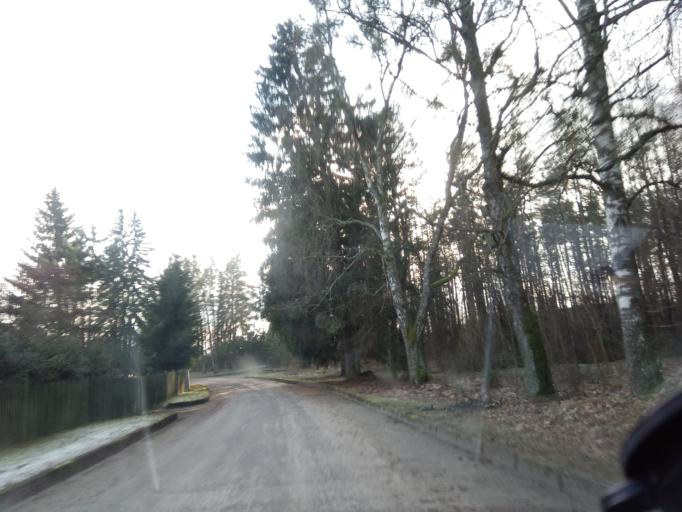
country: LT
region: Alytaus apskritis
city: Druskininkai
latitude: 53.9534
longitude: 24.2934
